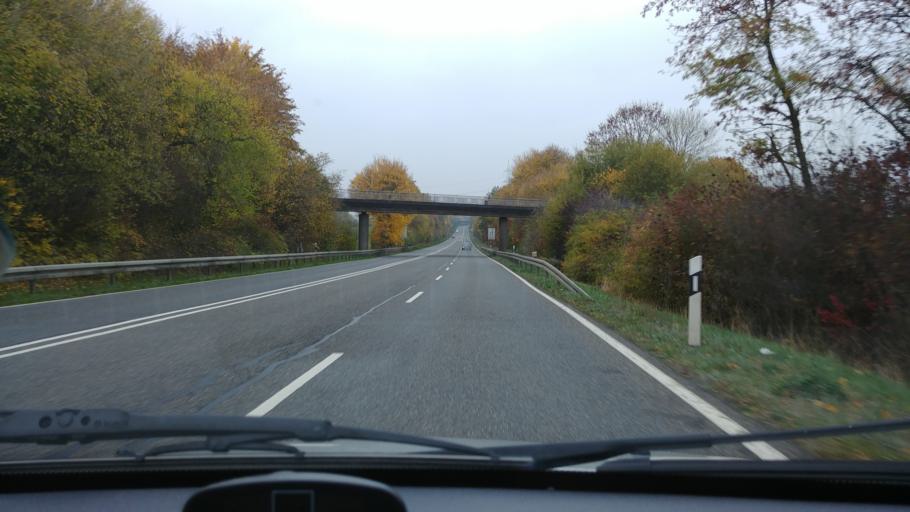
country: DE
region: Hesse
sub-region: Regierungsbezirk Giessen
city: Dehrn
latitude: 50.4574
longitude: 8.0786
